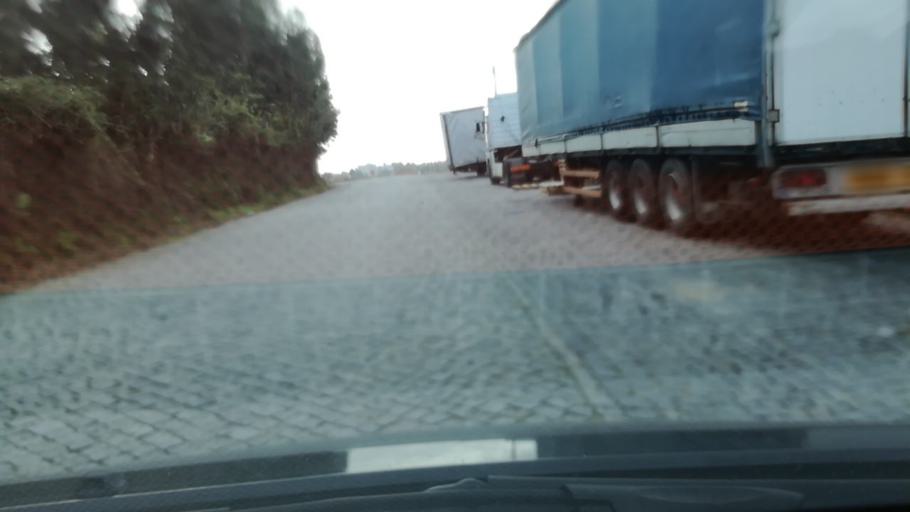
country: PT
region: Porto
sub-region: Maia
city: Gemunde
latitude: 41.2689
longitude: -8.6536
